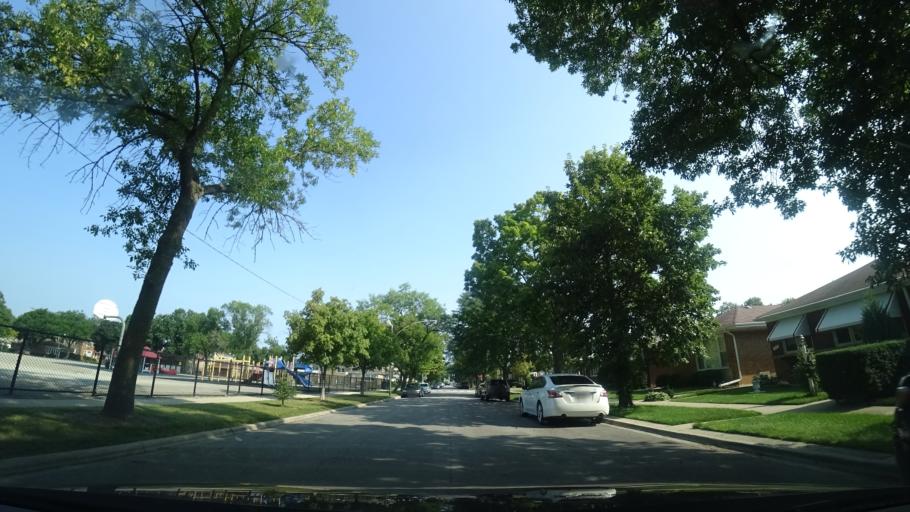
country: US
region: Illinois
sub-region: Cook County
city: Lincolnwood
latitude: 41.9947
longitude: -87.7239
